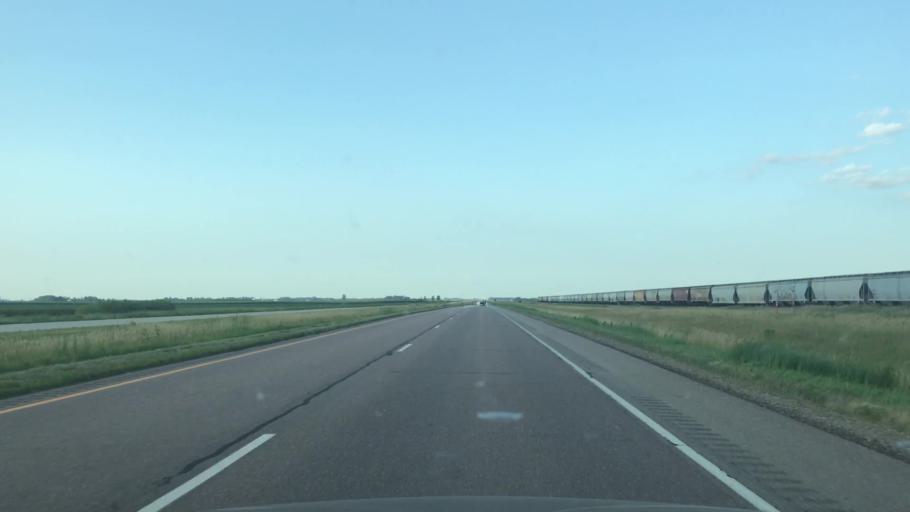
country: US
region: Minnesota
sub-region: Nobles County
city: Worthington
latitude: 43.7227
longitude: -95.4340
